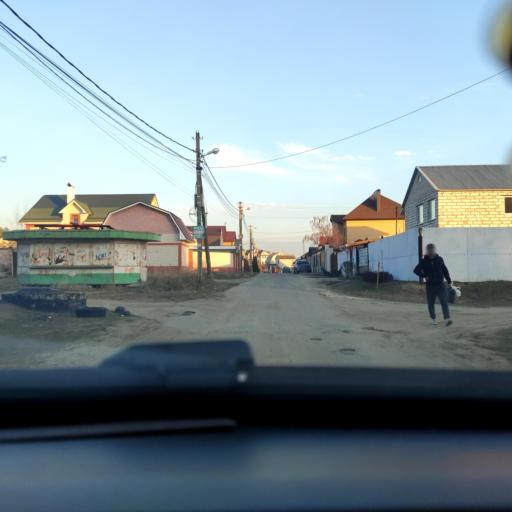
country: RU
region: Voronezj
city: Shilovo
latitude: 51.5780
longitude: 39.0438
